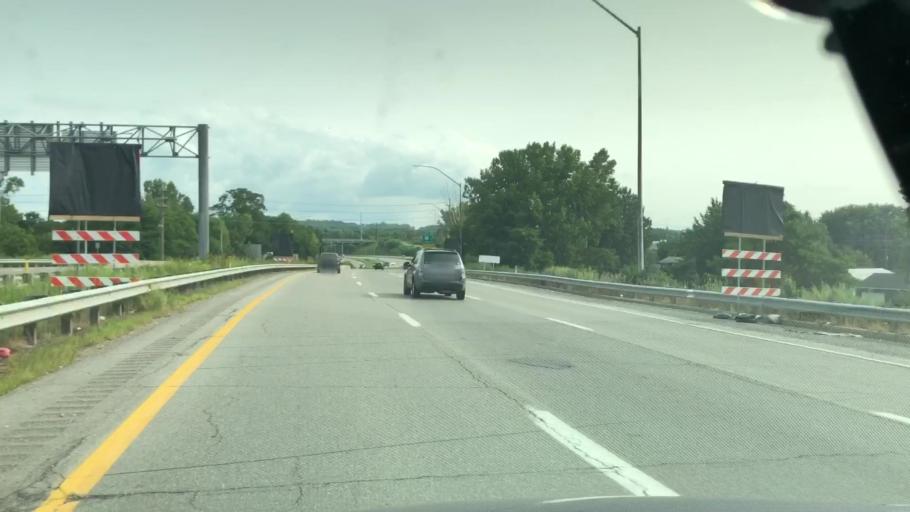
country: US
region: Pennsylvania
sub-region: Erie County
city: Erie
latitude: 42.1005
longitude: -80.1220
